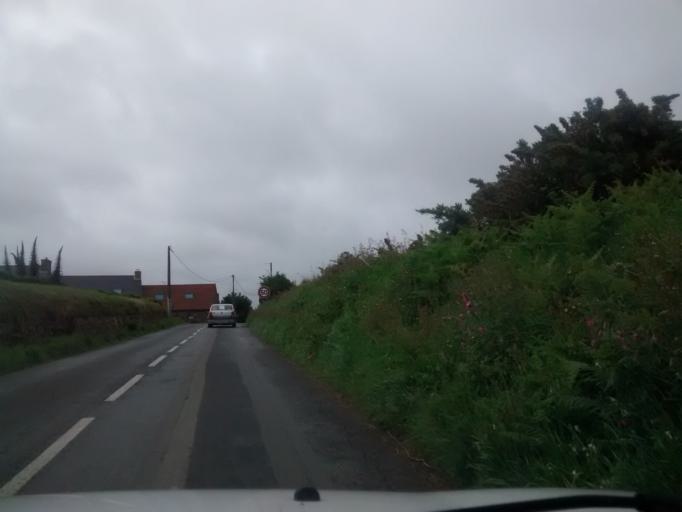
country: FR
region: Brittany
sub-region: Departement des Cotes-d'Armor
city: Plougrescant
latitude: 48.8345
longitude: -3.2347
